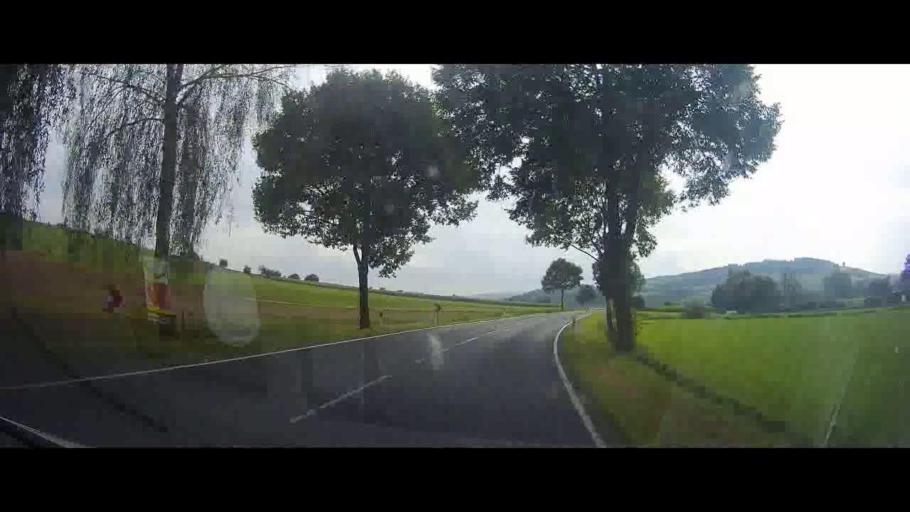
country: DE
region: Lower Saxony
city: Uslar
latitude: 51.6445
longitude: 9.6595
